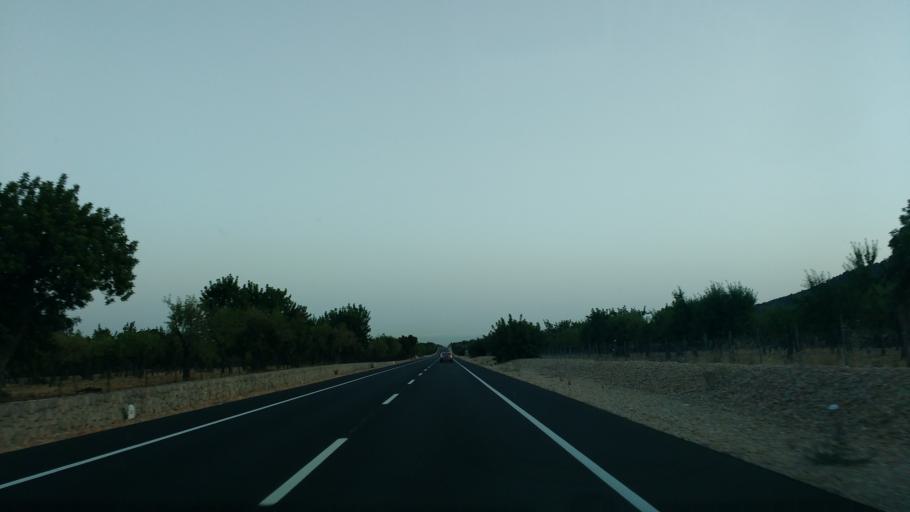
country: ES
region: Balearic Islands
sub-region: Illes Balears
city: Bunyola
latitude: 39.6840
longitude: 2.6825
